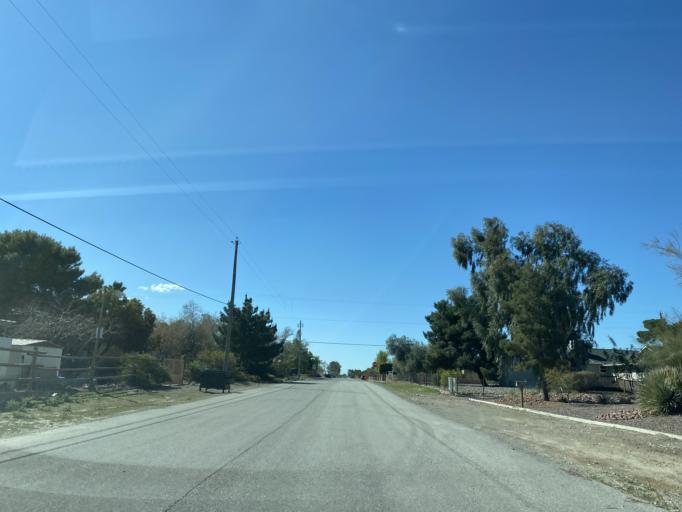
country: US
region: Nevada
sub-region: Clark County
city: North Las Vegas
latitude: 36.3330
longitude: -115.2852
